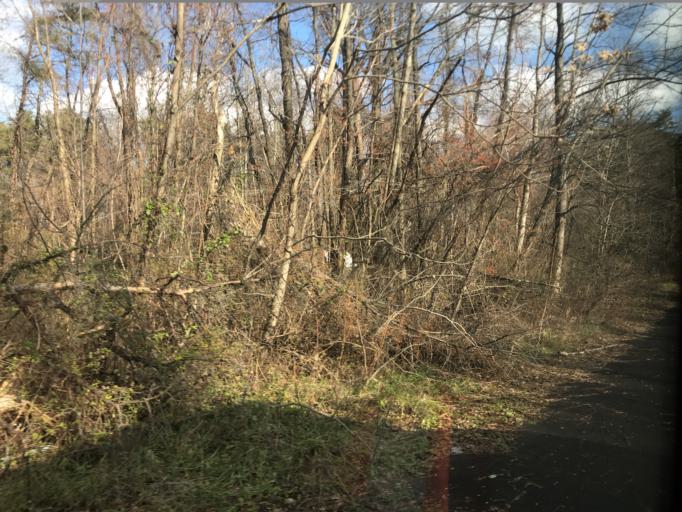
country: US
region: Pennsylvania
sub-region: Fulton County
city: McConnellsburg
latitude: 40.0490
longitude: -78.0966
